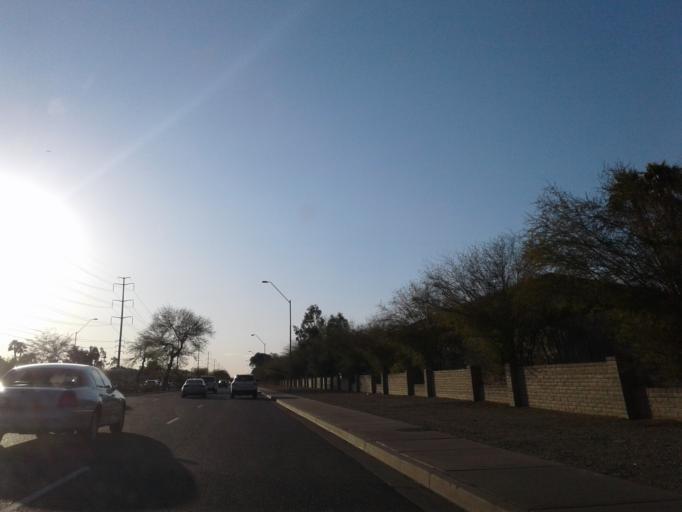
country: US
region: Arizona
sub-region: Maricopa County
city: Scottsdale
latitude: 33.5827
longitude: -111.8669
